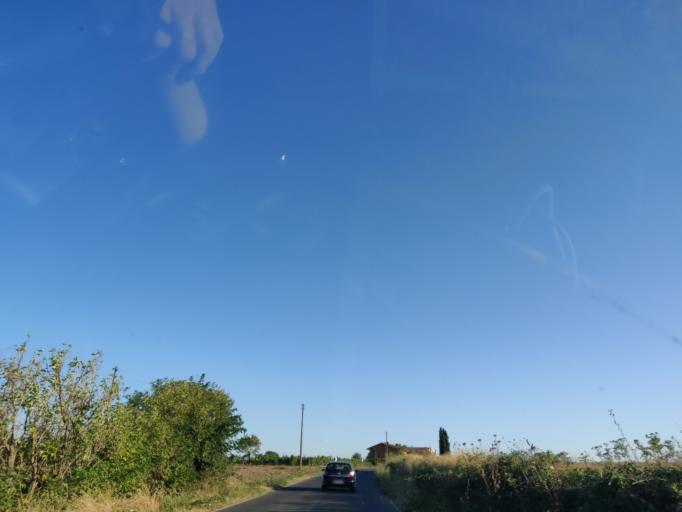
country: IT
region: Latium
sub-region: Provincia di Viterbo
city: Acquapendente
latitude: 42.7292
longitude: 11.8758
